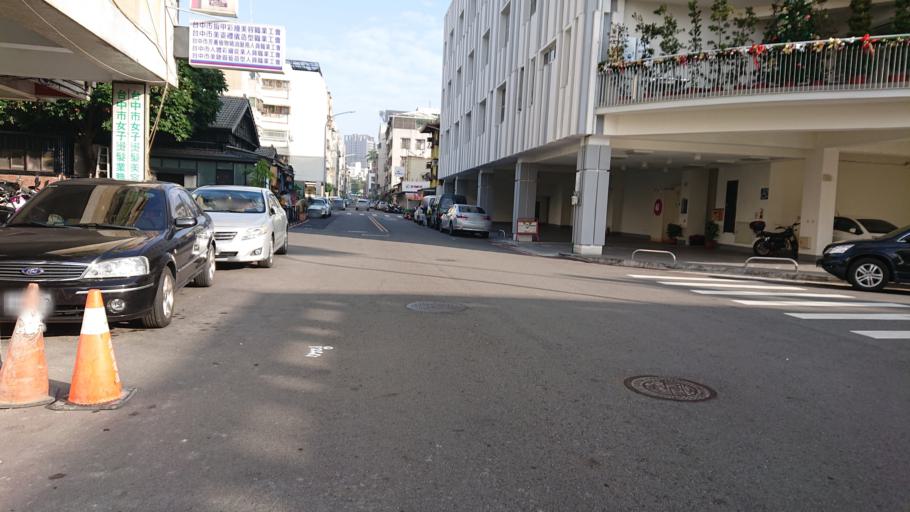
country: TW
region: Taiwan
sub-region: Taichung City
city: Taichung
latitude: 24.1473
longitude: 120.6676
